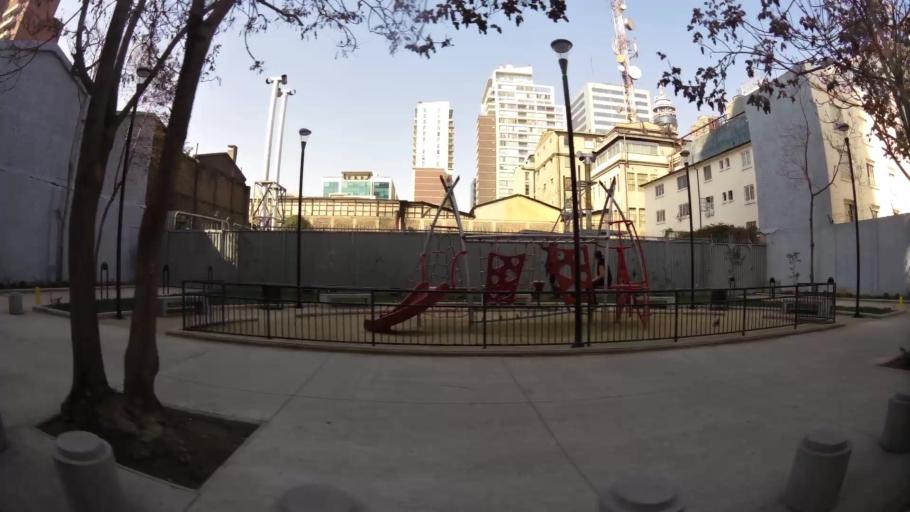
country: CL
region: Santiago Metropolitan
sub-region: Provincia de Santiago
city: Santiago
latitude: -33.4435
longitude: -70.6588
